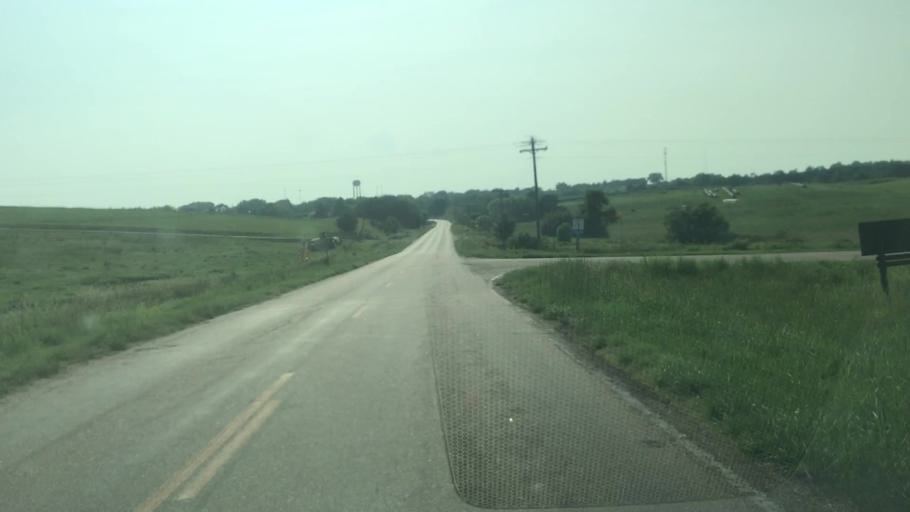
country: US
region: Nebraska
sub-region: Sherman County
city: Loup City
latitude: 41.2792
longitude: -98.9477
